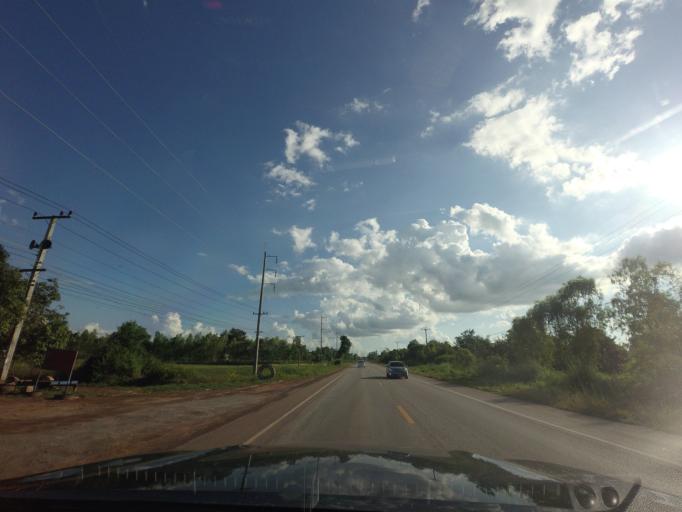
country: TH
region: Changwat Udon Thani
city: Thung Fon
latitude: 17.4951
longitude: 103.2007
